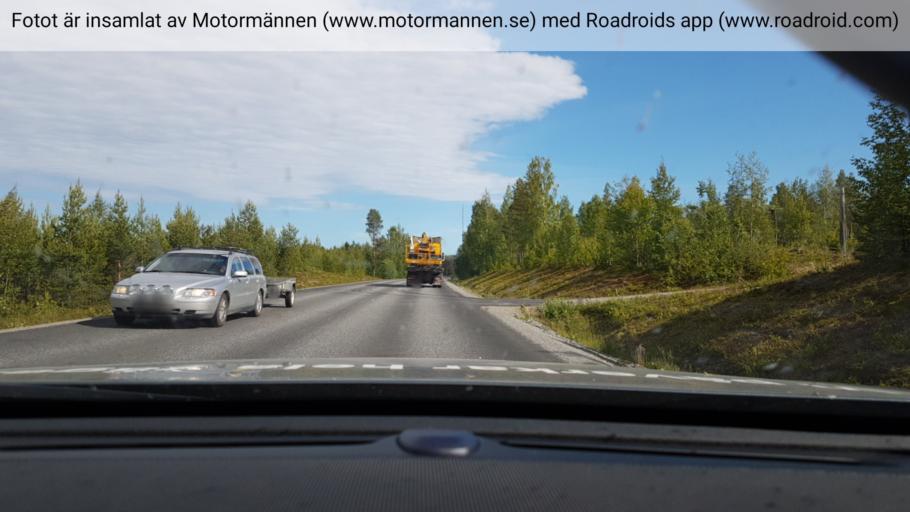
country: SE
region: Vaesterbotten
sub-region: Lycksele Kommun
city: Soderfors
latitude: 64.8357
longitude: 17.9974
